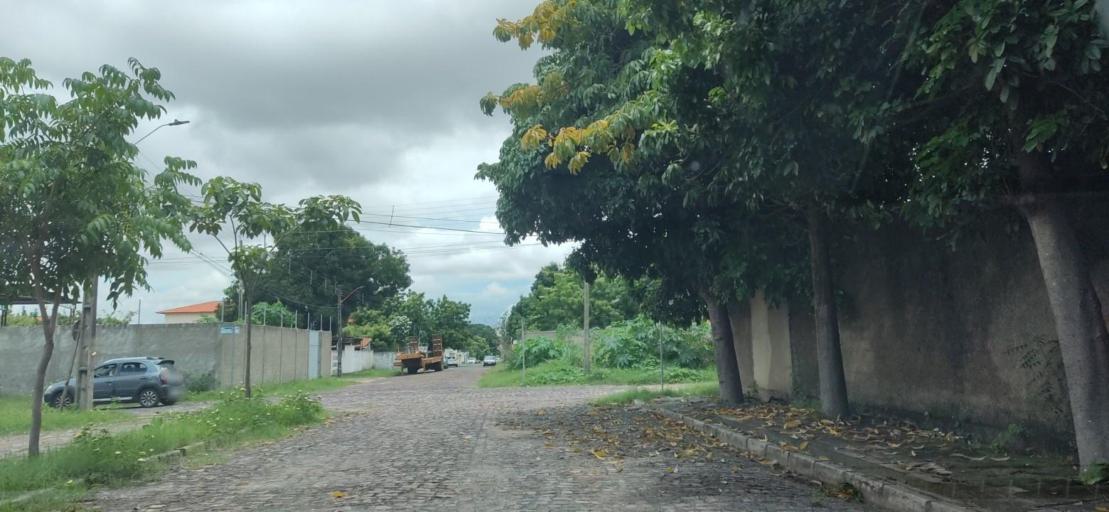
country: BR
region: Piaui
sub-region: Teresina
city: Teresina
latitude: -5.0751
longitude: -42.7621
